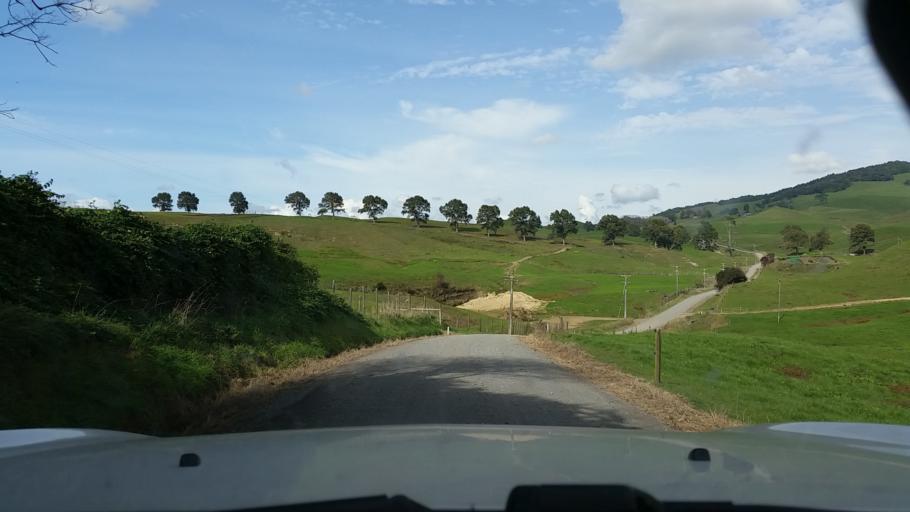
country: NZ
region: Waikato
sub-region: Matamata-Piako District
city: Matamata
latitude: -37.8097
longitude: 175.6728
